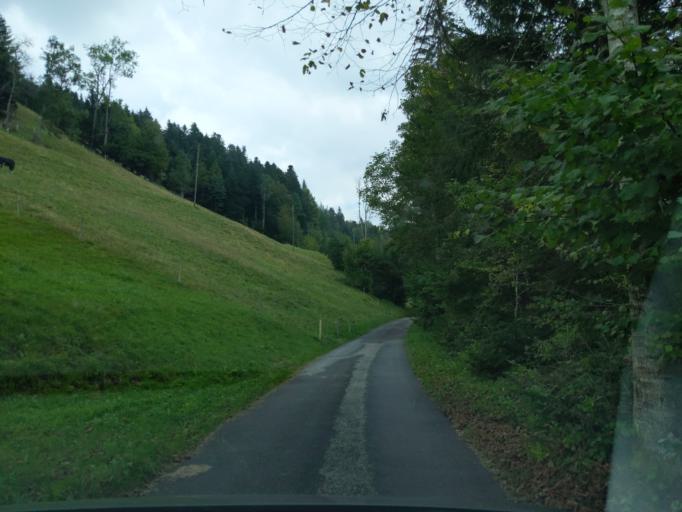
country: CH
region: Bern
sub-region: Oberaargau
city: Wyssachen
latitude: 47.0405
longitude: 7.8248
